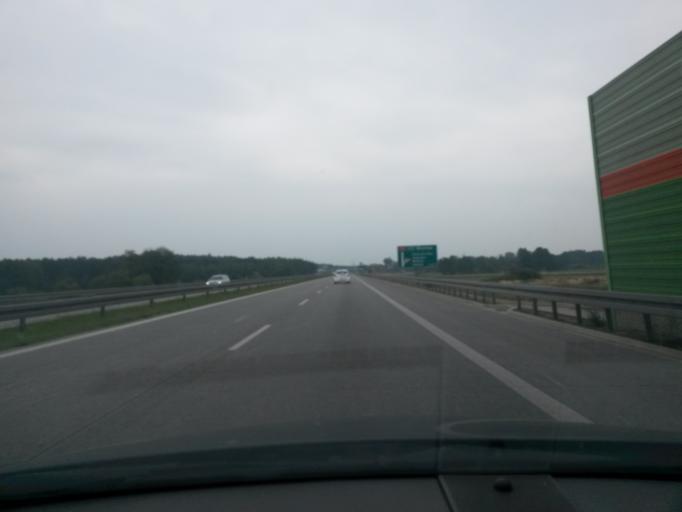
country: PL
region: Lodz Voivodeship
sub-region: Powiat tomaszowski
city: Tomaszow Mazowiecki
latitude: 51.5324
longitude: 19.9517
